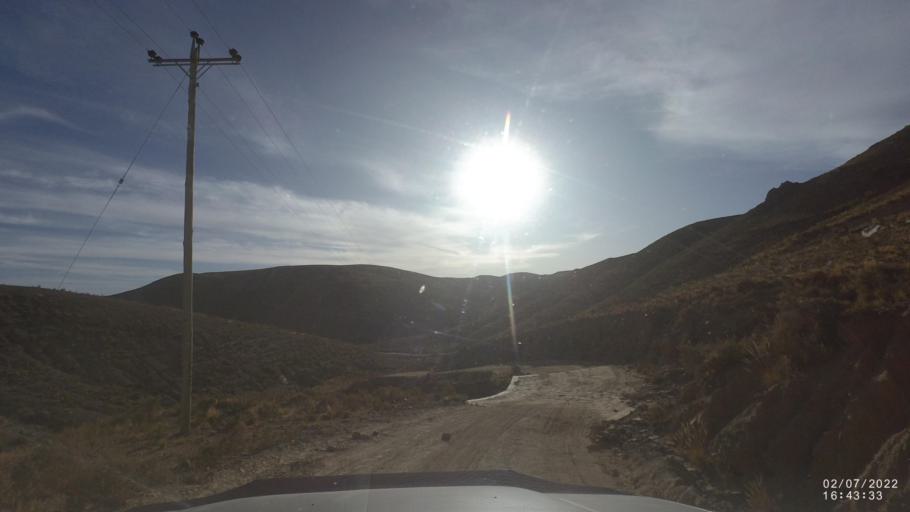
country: BO
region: Cochabamba
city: Irpa Irpa
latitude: -17.9726
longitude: -66.5063
